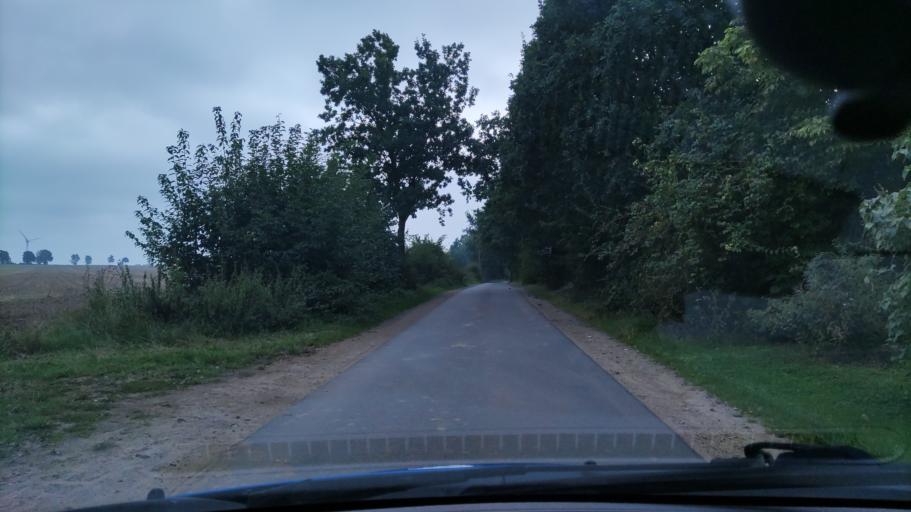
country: DE
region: Lower Saxony
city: Altenmedingen
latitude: 53.1302
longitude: 10.6073
